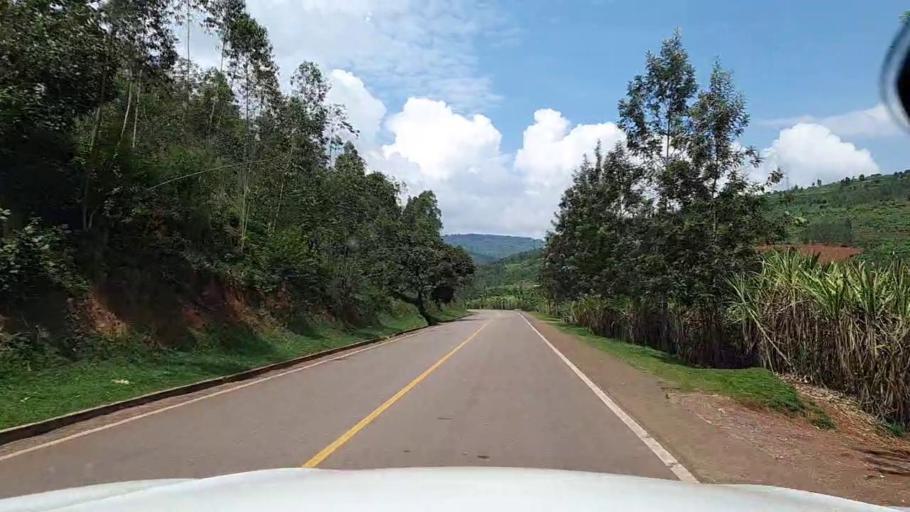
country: RW
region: Kigali
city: Kigali
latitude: -1.8446
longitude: 30.0938
